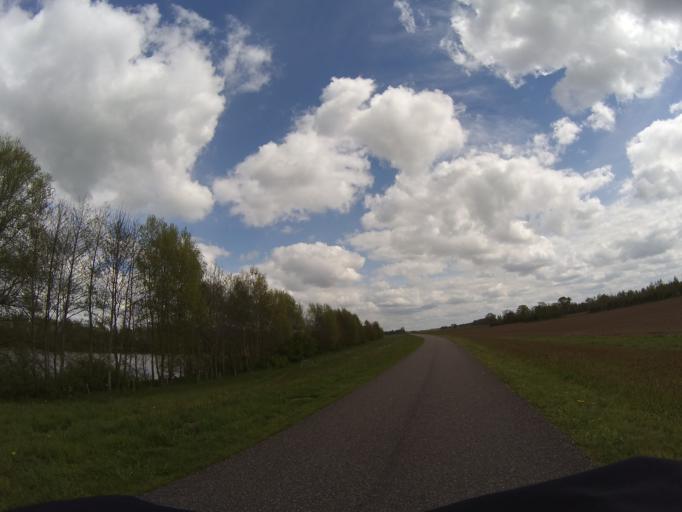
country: NL
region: Overijssel
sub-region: Gemeente Dalfsen
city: Dalfsen
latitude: 52.5210
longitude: 6.1843
